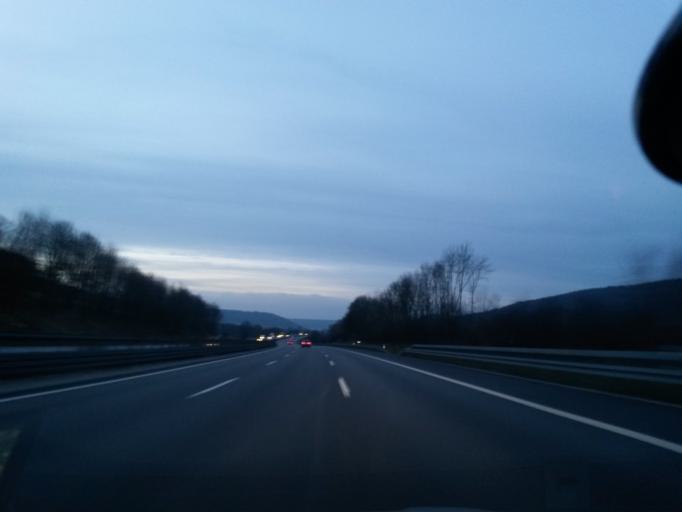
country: DE
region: Bavaria
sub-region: Regierungsbezirk Mittelfranken
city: Thalmassing
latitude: 49.1104
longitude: 11.2798
